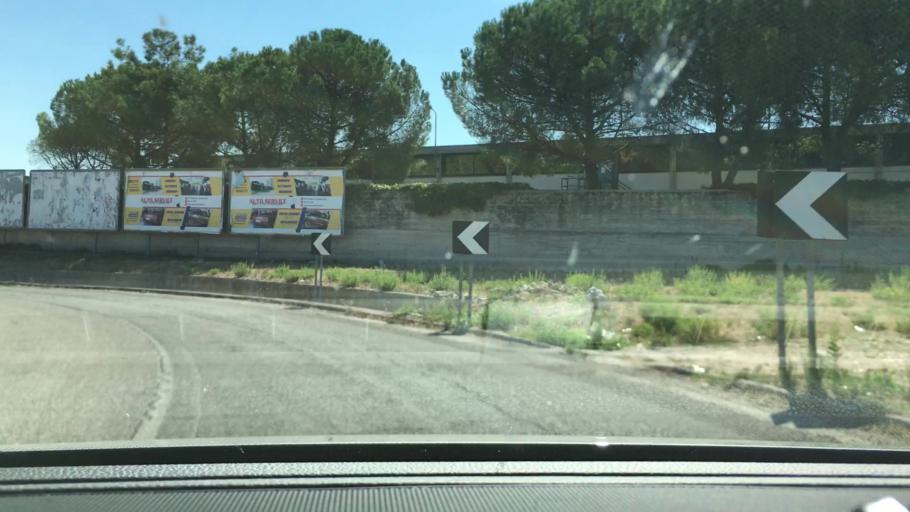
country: IT
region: Apulia
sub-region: Provincia di Bari
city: Bitritto
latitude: 41.0715
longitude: 16.8281
